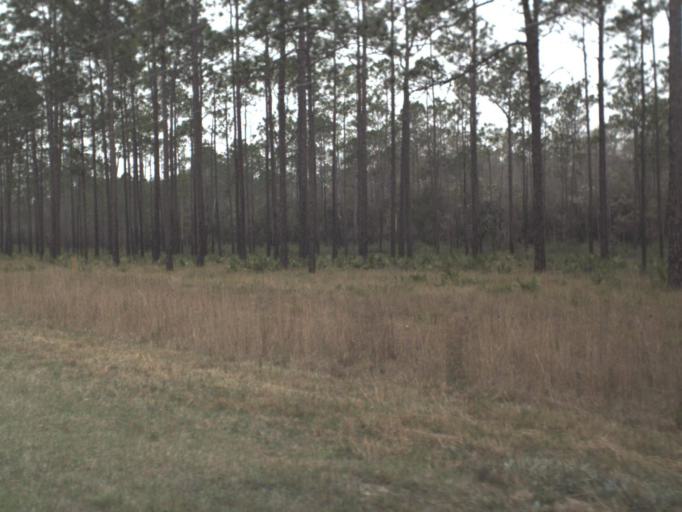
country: US
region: Florida
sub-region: Liberty County
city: Bristol
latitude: 30.2550
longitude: -84.8581
